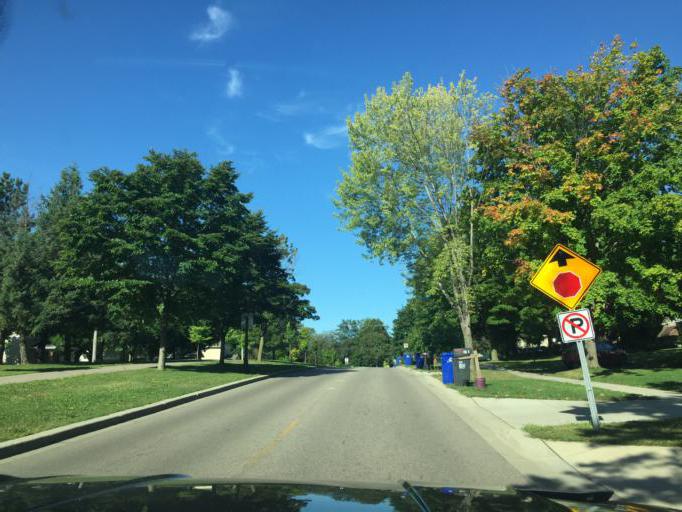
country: US
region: Minnesota
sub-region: Ramsey County
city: Little Canada
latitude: 44.9907
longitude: -93.0946
